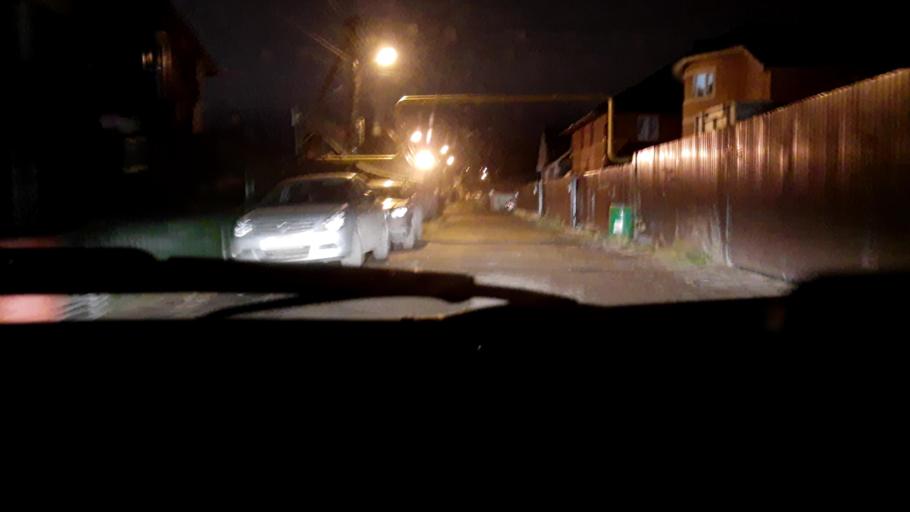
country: RU
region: Bashkortostan
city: Ufa
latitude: 54.7059
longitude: 55.9408
